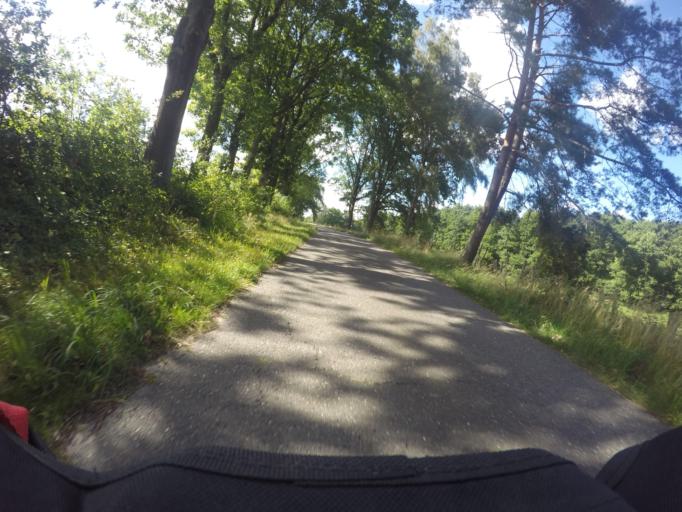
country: DE
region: Lower Saxony
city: Thomasburg
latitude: 53.2256
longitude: 10.6615
